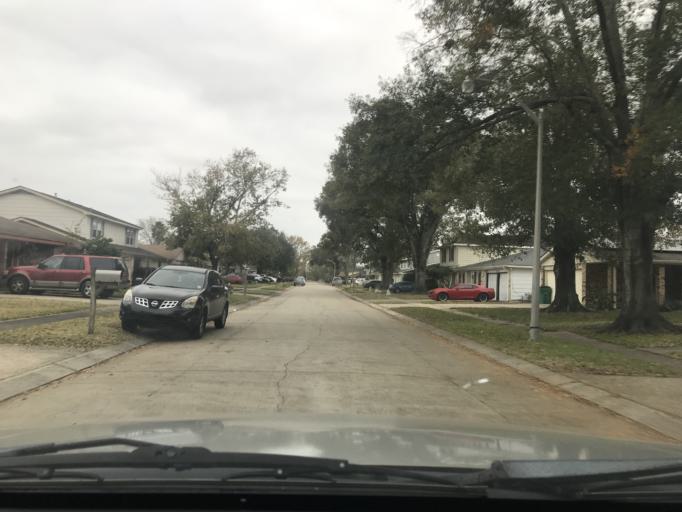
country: US
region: Louisiana
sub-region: Jefferson Parish
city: Woodmere
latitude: 29.8652
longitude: -90.0789
